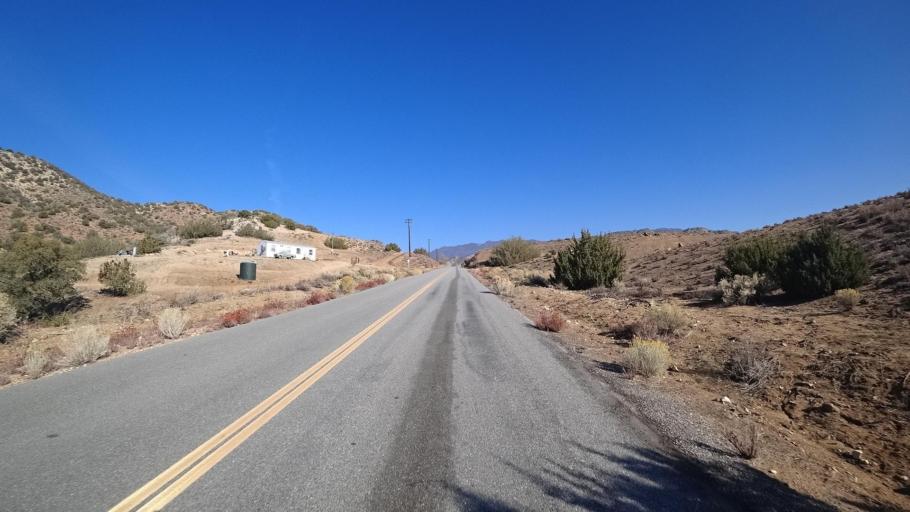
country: US
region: California
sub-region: Kern County
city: Tehachapi
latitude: 35.3462
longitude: -118.3867
